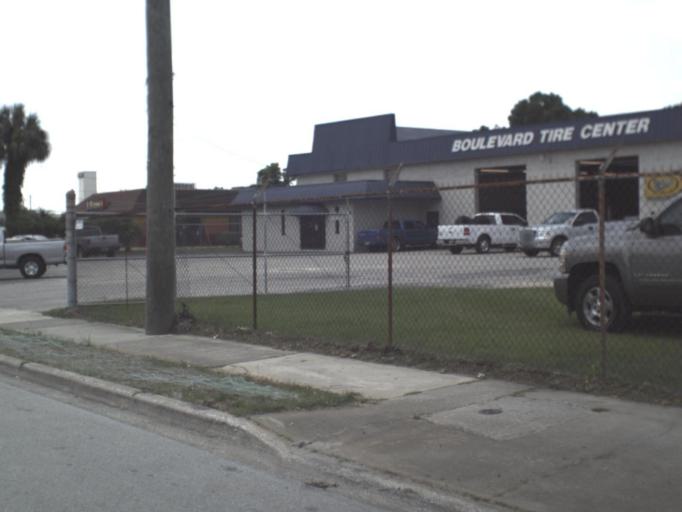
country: US
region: Florida
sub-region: Duval County
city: Jacksonville
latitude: 30.3339
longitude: -81.7311
